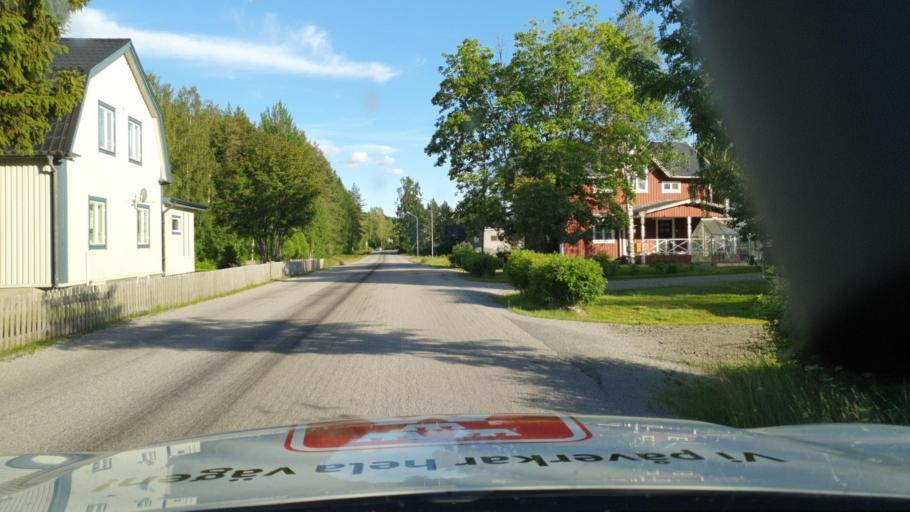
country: SE
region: Vaesterbotten
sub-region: Vindelns Kommun
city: Vindeln
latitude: 64.1547
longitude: 19.5085
